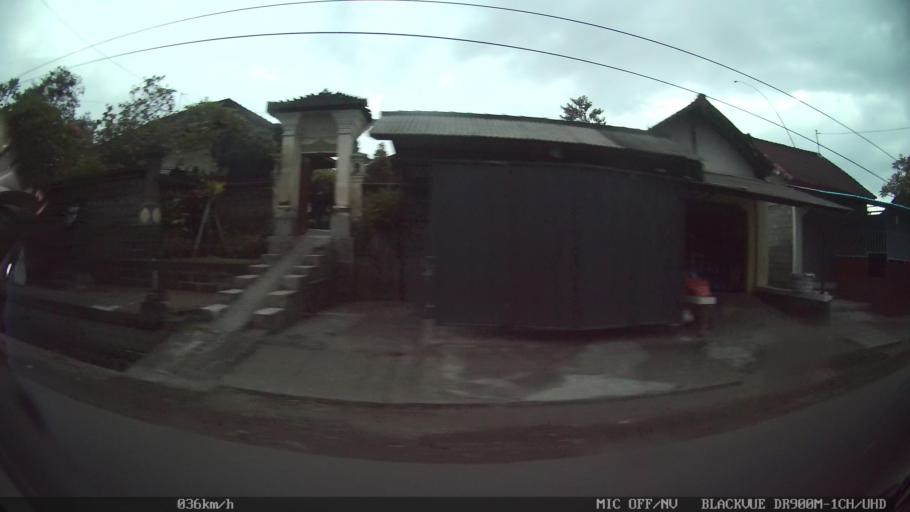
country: ID
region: Bali
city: Banjar Kertajiwa
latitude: -8.6346
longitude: 115.2614
